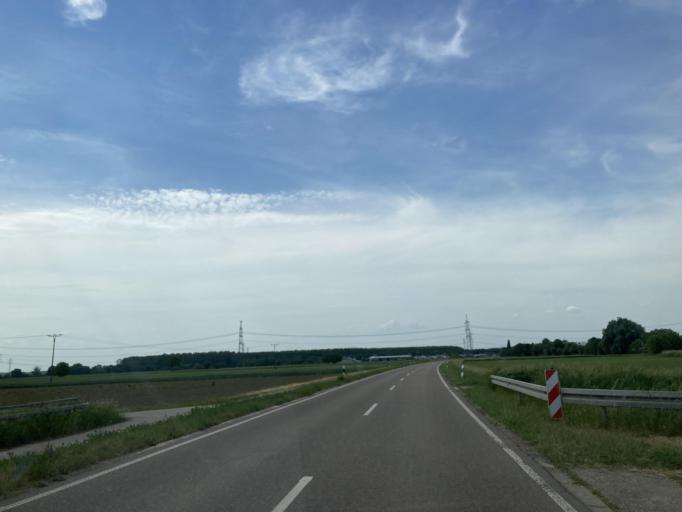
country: DE
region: Baden-Wuerttemberg
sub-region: Karlsruhe Region
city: Graben-Neudorf
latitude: 49.1741
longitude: 8.4433
